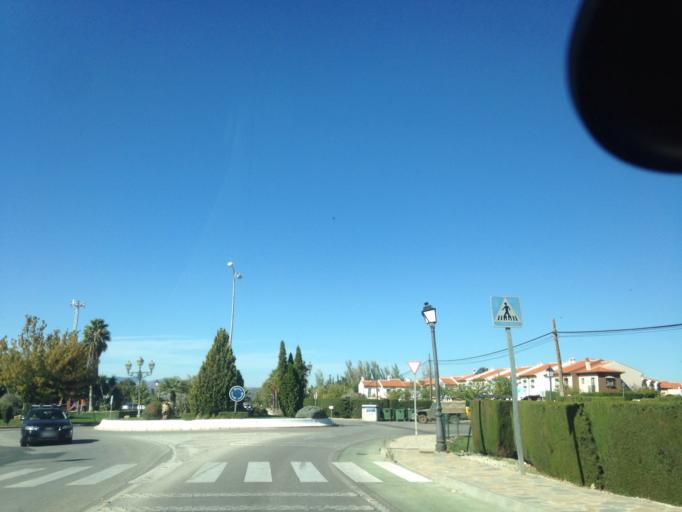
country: ES
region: Andalusia
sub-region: Provincia de Malaga
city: Ronda
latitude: 36.7274
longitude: -5.1517
